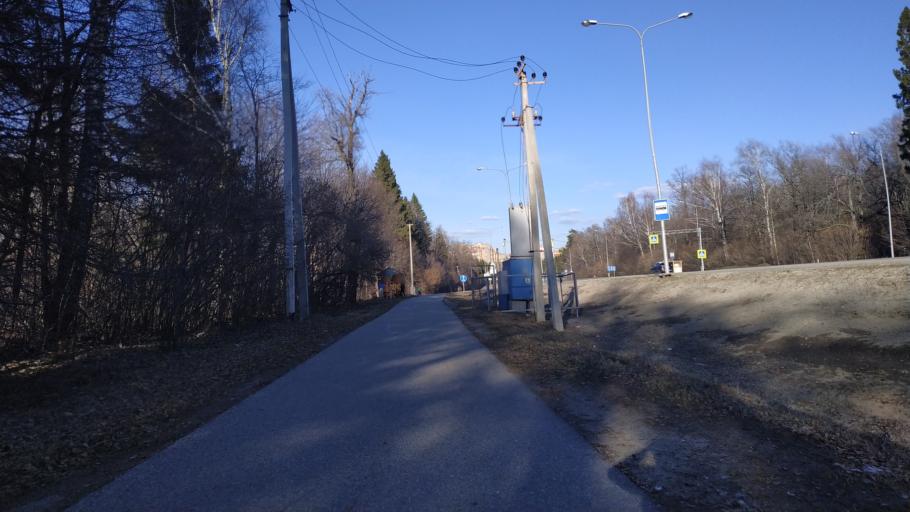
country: RU
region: Chuvashia
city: Novyye Lapsary
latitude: 56.1303
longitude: 47.1357
